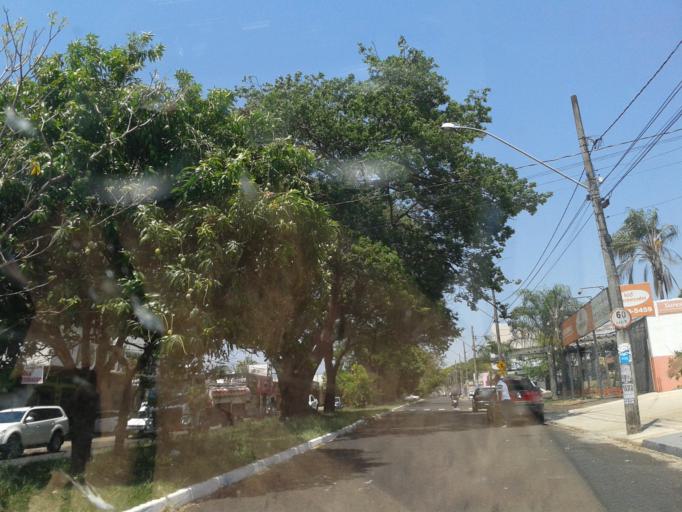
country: BR
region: Minas Gerais
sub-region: Uberlandia
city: Uberlandia
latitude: -18.9330
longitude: -48.3032
